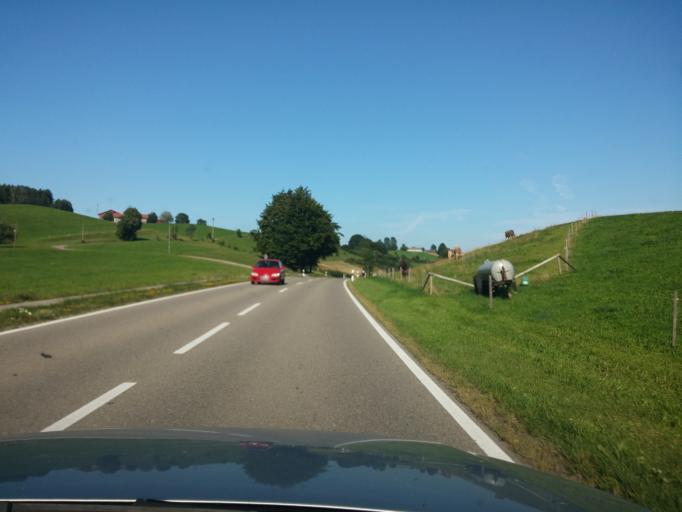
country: DE
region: Bavaria
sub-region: Swabia
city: Altusried
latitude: 47.8099
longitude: 10.1853
